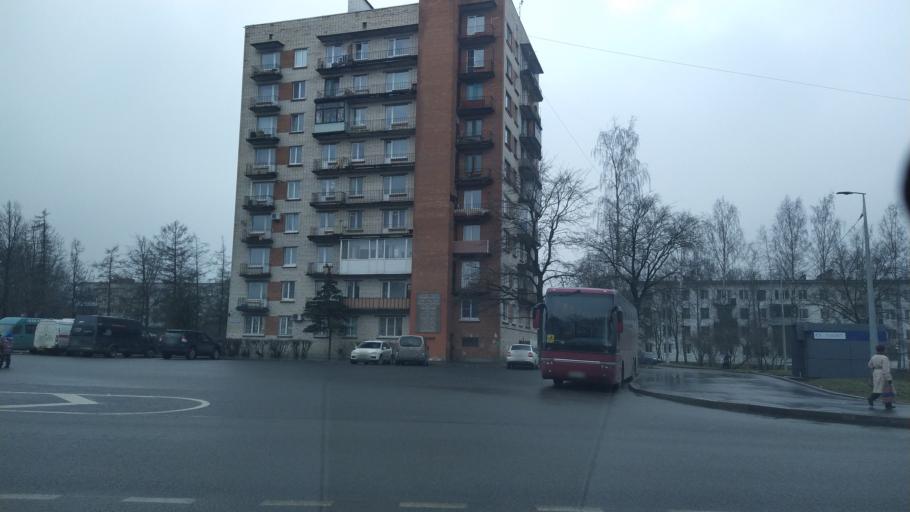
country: RU
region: St.-Petersburg
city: Krasnoye Selo
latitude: 59.7342
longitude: 30.0887
